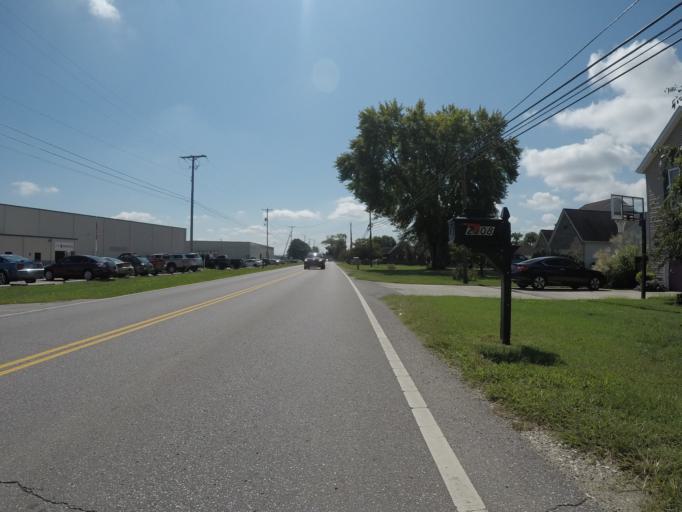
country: US
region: Ohio
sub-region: Lawrence County
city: South Point
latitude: 38.4328
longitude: -82.5948
